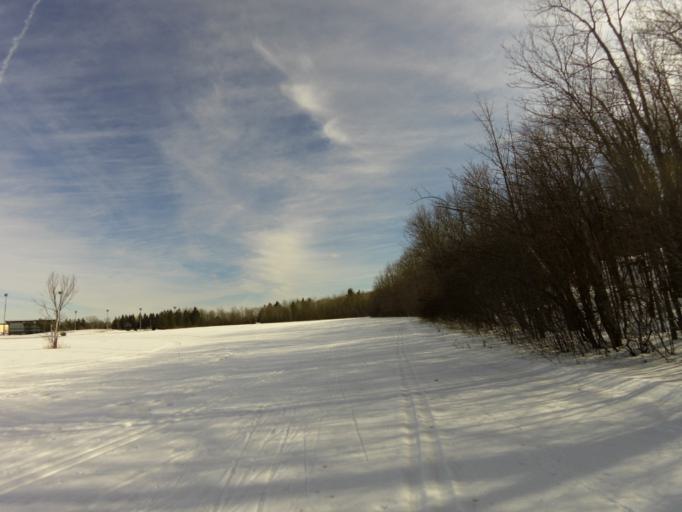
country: CA
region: Quebec
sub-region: Outaouais
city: Gatineau
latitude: 45.4615
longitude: -75.7787
